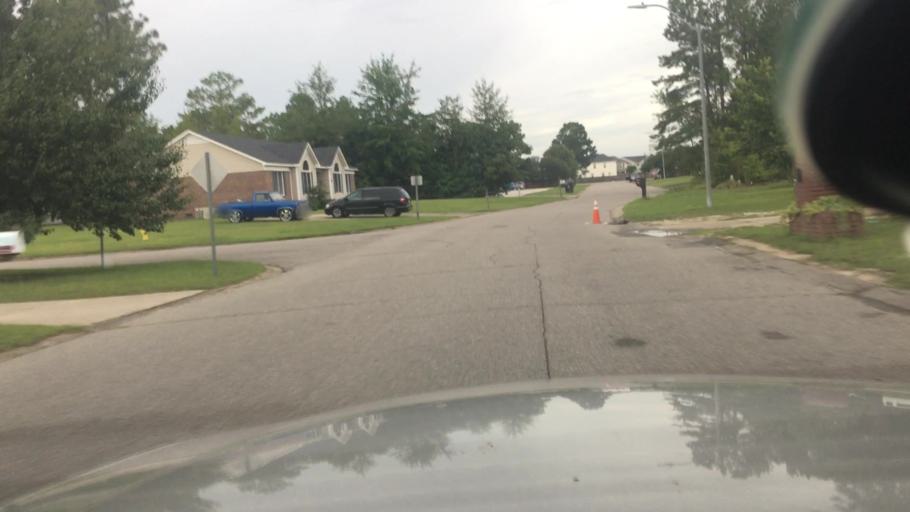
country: US
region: North Carolina
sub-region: Cumberland County
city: Hope Mills
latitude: 34.9736
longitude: -78.9764
